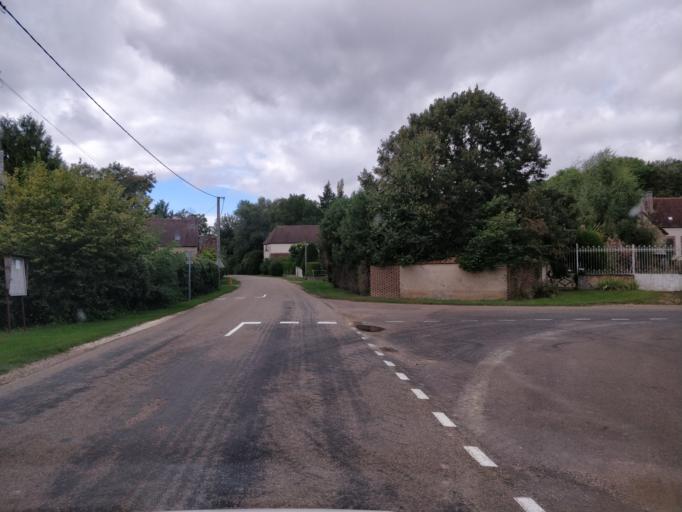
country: FR
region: Champagne-Ardenne
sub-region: Departement de l'Aube
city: Aix-en-Othe
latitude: 48.1603
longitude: 3.6354
